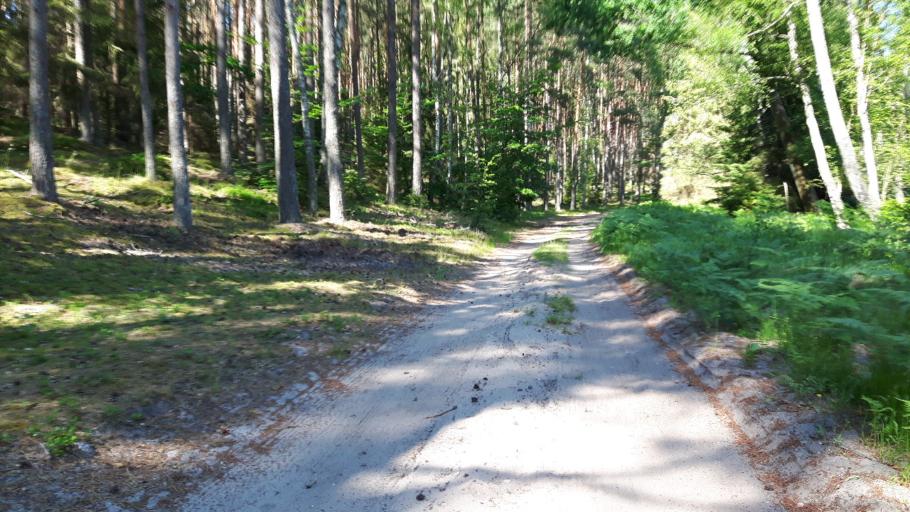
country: PL
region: Pomeranian Voivodeship
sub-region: Powiat leborski
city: Leba
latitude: 54.6960
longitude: 17.4749
